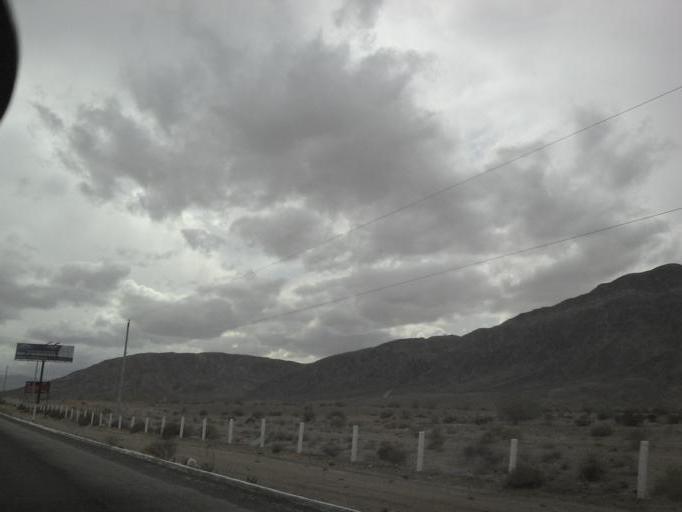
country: MX
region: Baja California
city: Progreso
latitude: 32.5918
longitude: -115.6939
